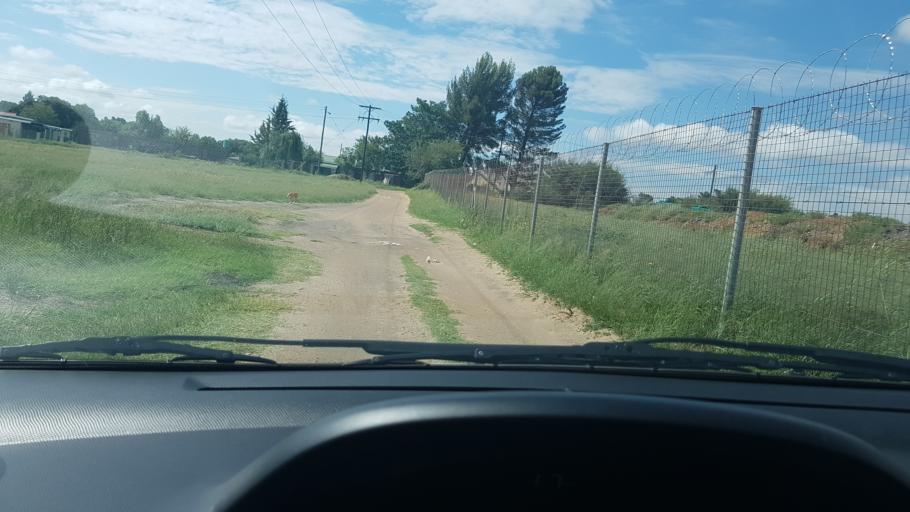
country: ZA
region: Northern Cape
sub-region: Siyanda District Municipality
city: Danielskuil
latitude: -28.1883
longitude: 23.5385
